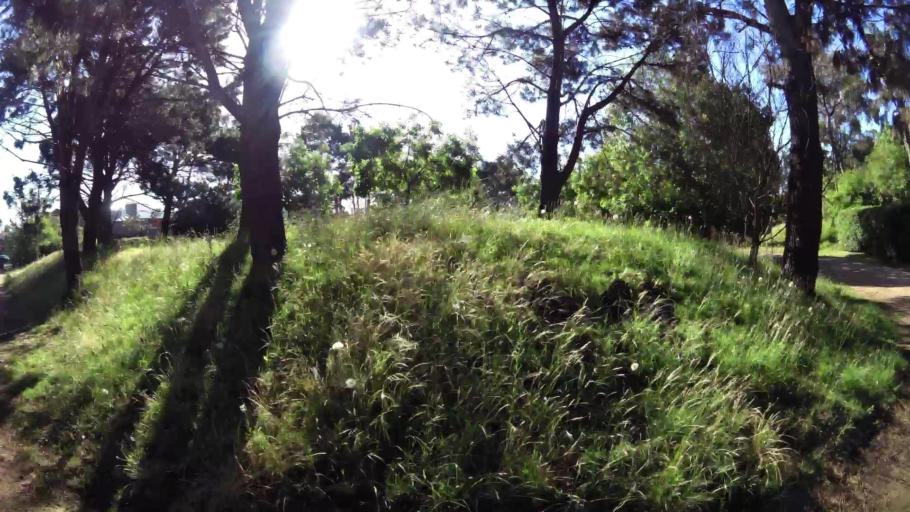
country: UY
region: Canelones
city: Barra de Carrasco
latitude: -34.8612
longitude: -56.0285
